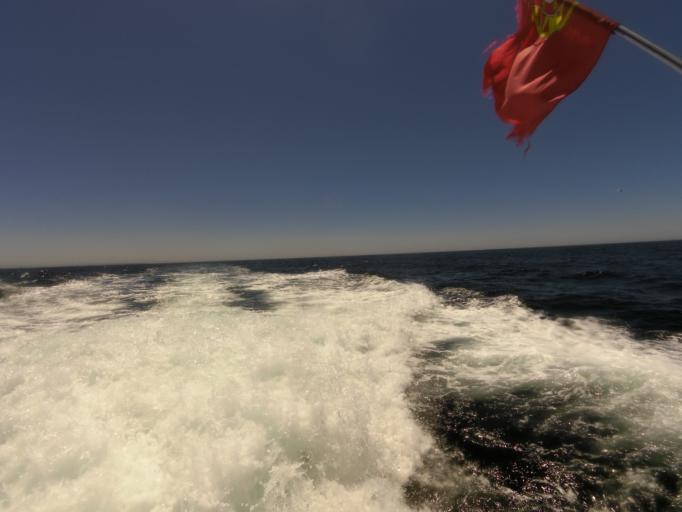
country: PT
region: Leiria
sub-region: Peniche
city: Peniche
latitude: 39.4094
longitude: -9.5006
